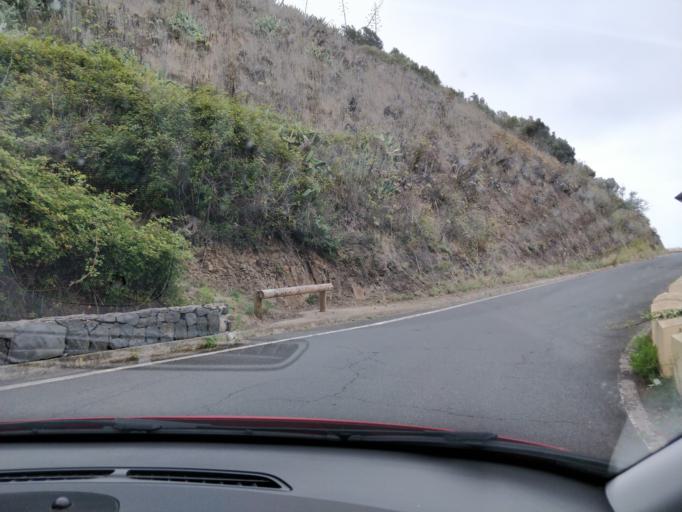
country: ES
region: Canary Islands
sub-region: Provincia de Santa Cruz de Tenerife
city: Santiago del Teide
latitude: 28.3230
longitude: -16.8506
